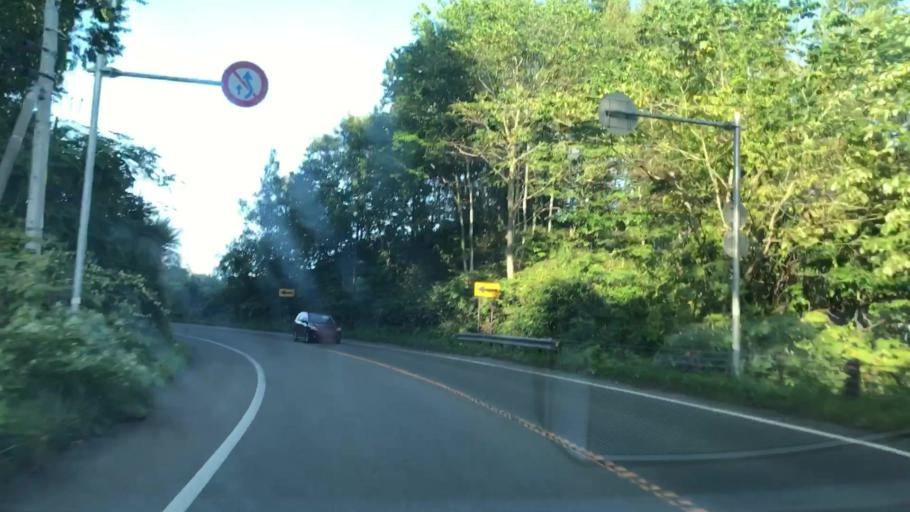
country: JP
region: Hokkaido
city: Date
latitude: 42.6087
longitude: 140.7764
